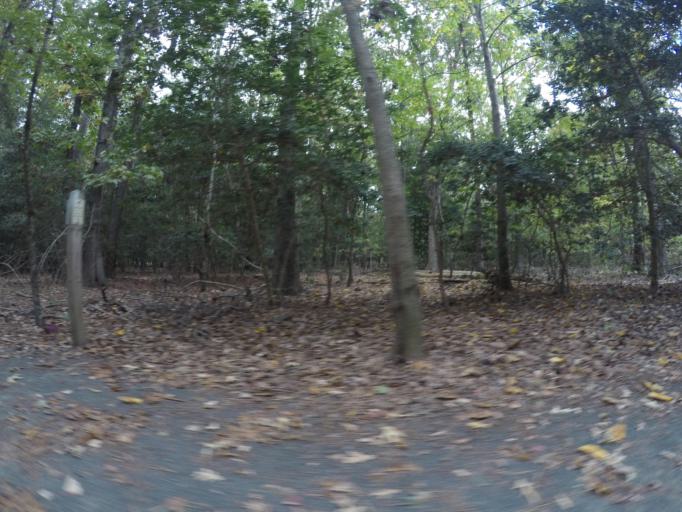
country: US
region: Delaware
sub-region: Sussex County
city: Rehoboth Beach
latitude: 38.7186
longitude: -75.1053
